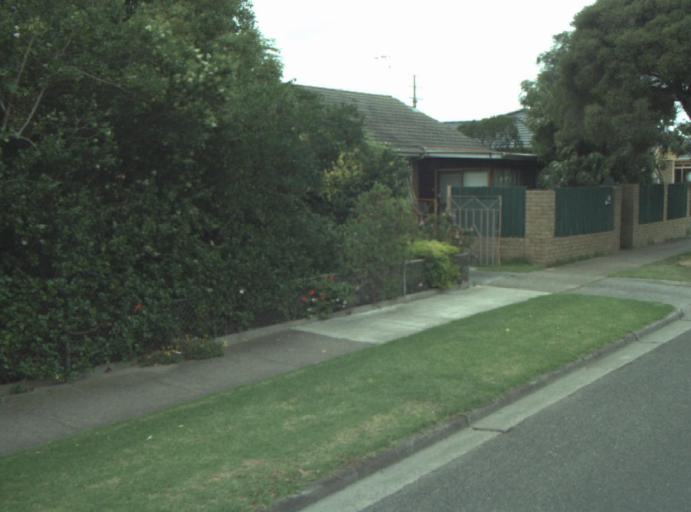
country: AU
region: Victoria
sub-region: Greater Geelong
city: Bell Park
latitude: -38.0818
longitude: 144.3467
